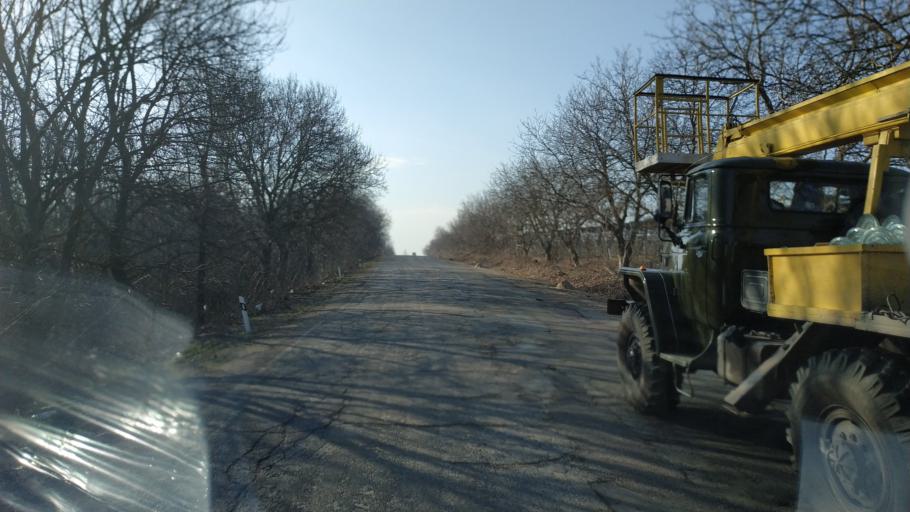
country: MD
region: Chisinau
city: Singera
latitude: 46.8620
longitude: 29.0317
